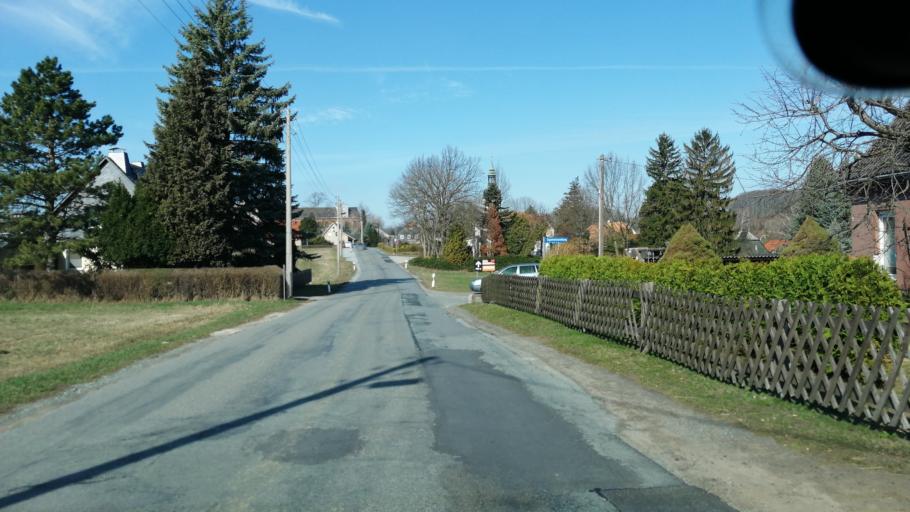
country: DE
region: Saxony
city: Schonbach
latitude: 51.0592
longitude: 14.5757
